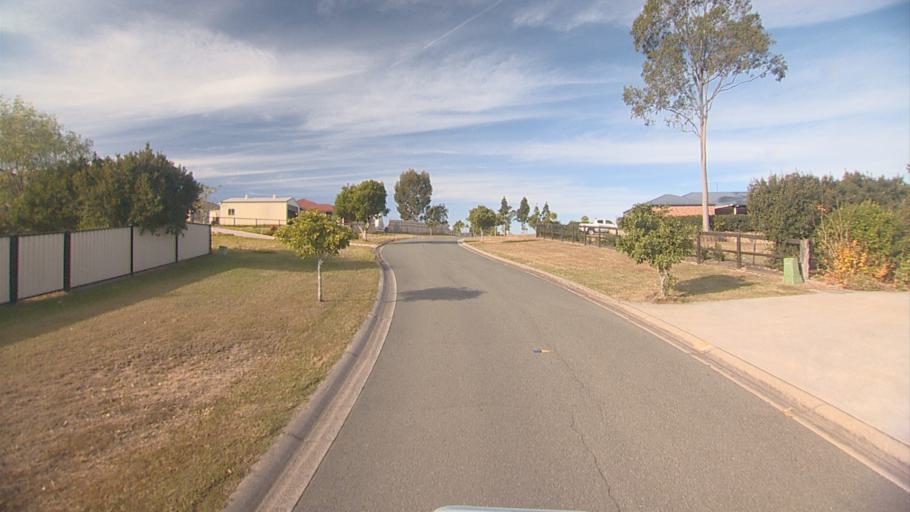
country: AU
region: Queensland
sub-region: Logan
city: North Maclean
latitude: -27.7982
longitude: 152.9577
